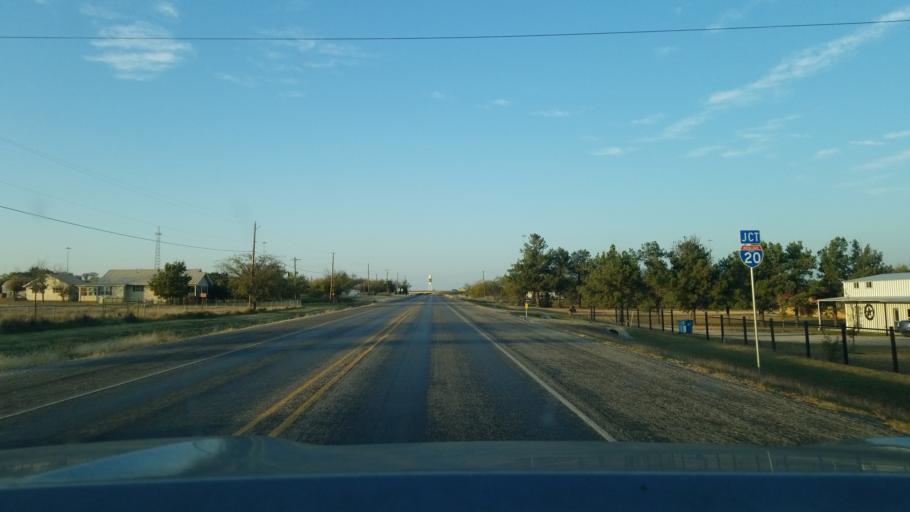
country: US
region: Texas
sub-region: Eastland County
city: Cisco
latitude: 32.3692
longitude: -98.9702
